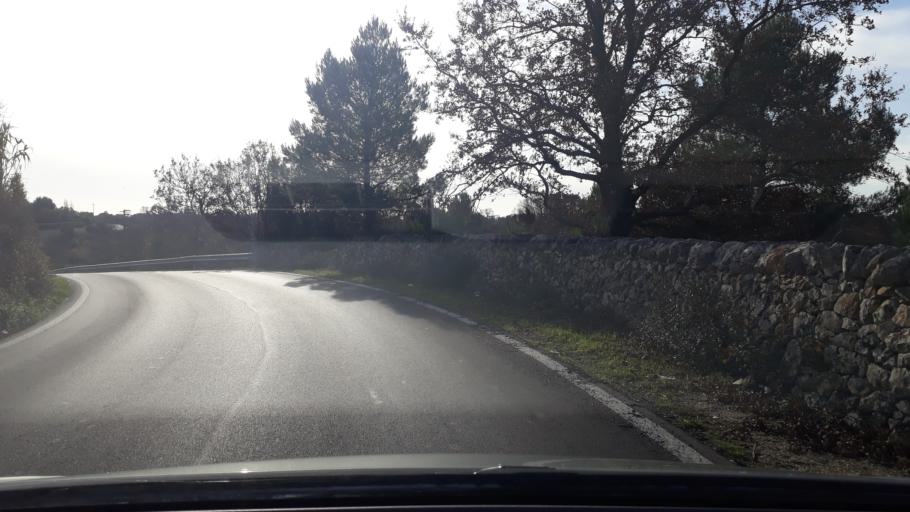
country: IT
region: Apulia
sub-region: Provincia di Taranto
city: Martina Franca
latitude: 40.6860
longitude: 17.3504
